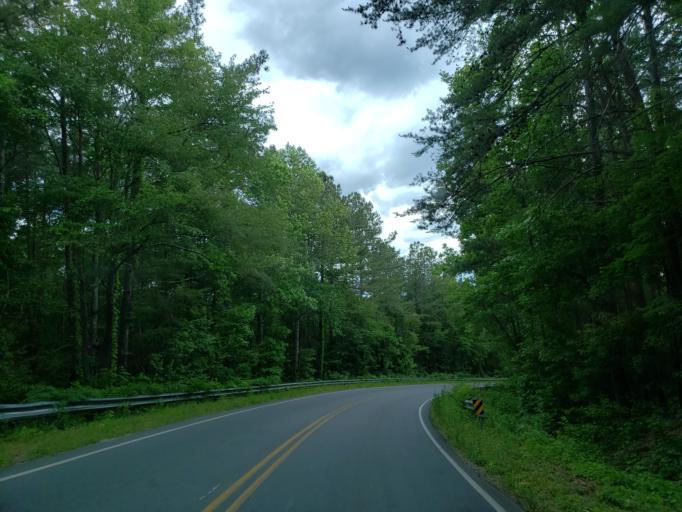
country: US
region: Georgia
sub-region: Polk County
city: Rockmart
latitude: 33.9622
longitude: -85.0504
